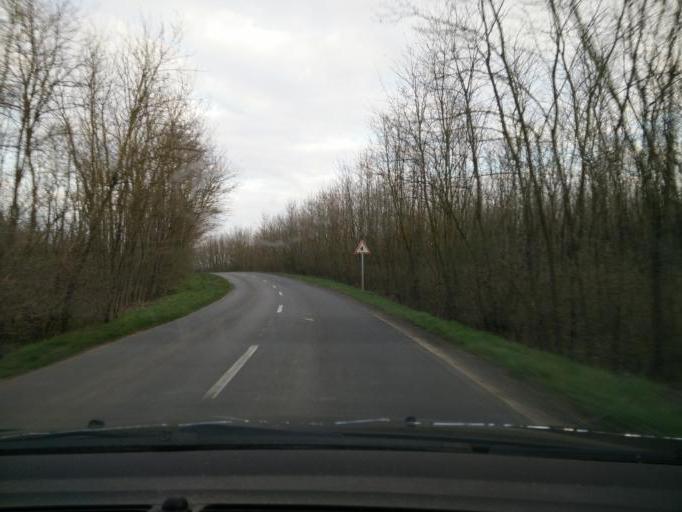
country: HU
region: Zala
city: Turje
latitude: 46.9882
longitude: 17.0705
